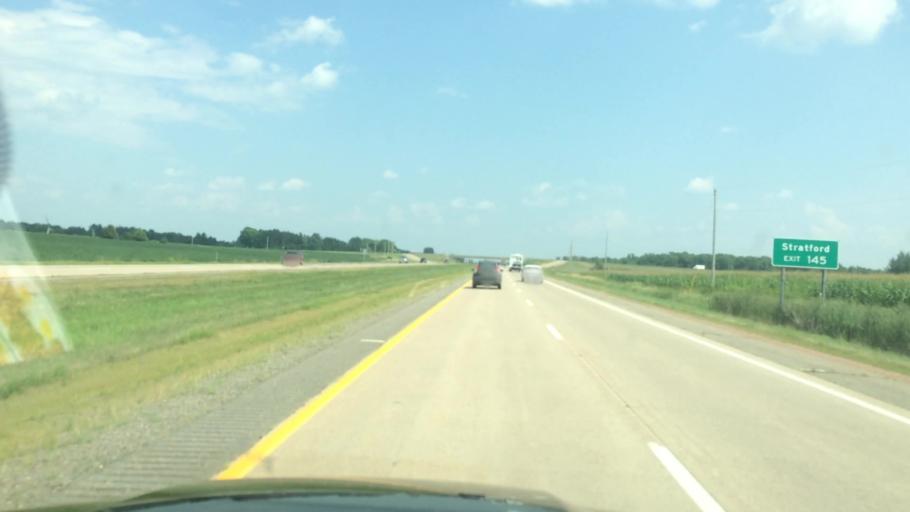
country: US
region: Wisconsin
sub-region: Marathon County
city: Athens
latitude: 44.9451
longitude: -90.0882
